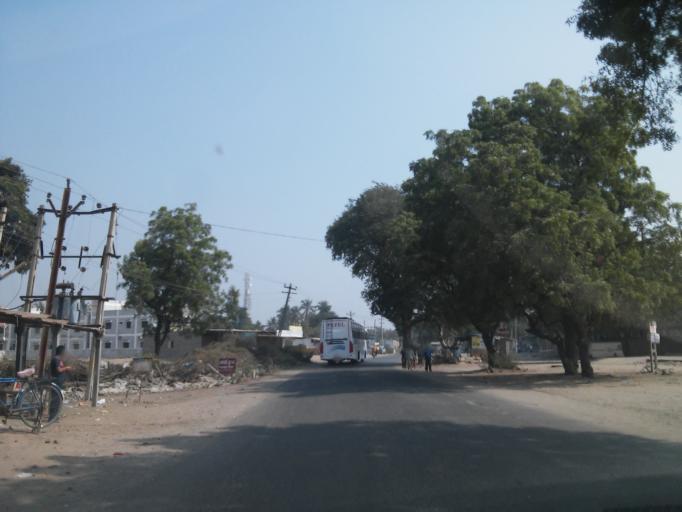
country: IN
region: Gujarat
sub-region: Kachchh
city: Mundra
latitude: 22.8398
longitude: 69.7126
